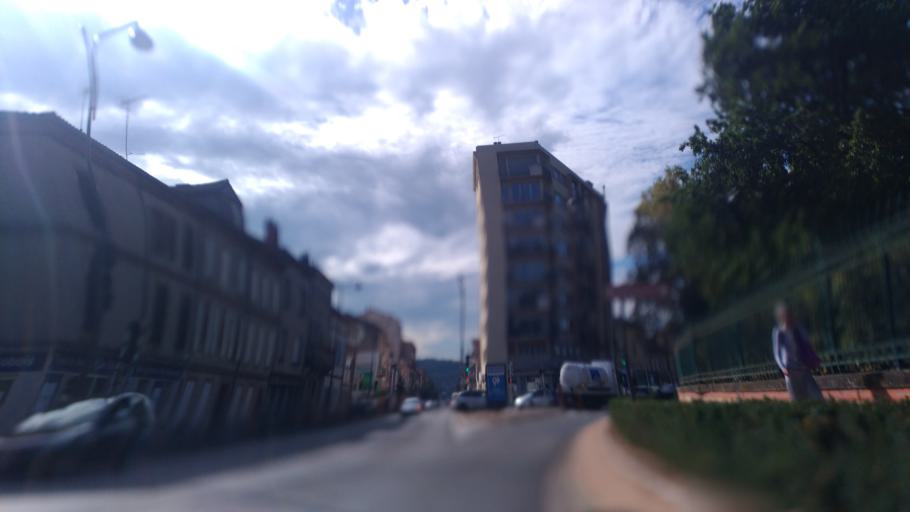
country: FR
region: Midi-Pyrenees
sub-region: Departement du Tarn
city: Albi
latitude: 43.9215
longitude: 2.1464
